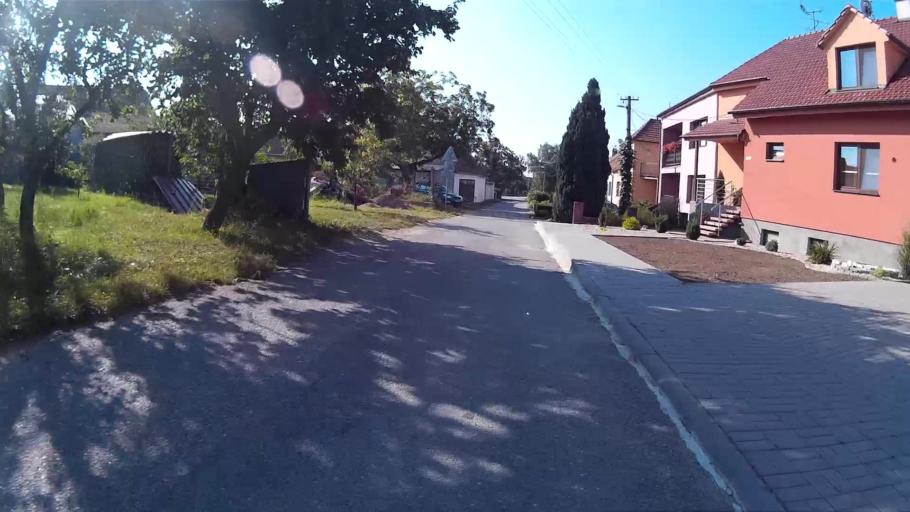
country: CZ
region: South Moravian
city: Vranovice
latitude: 48.9329
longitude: 16.5761
